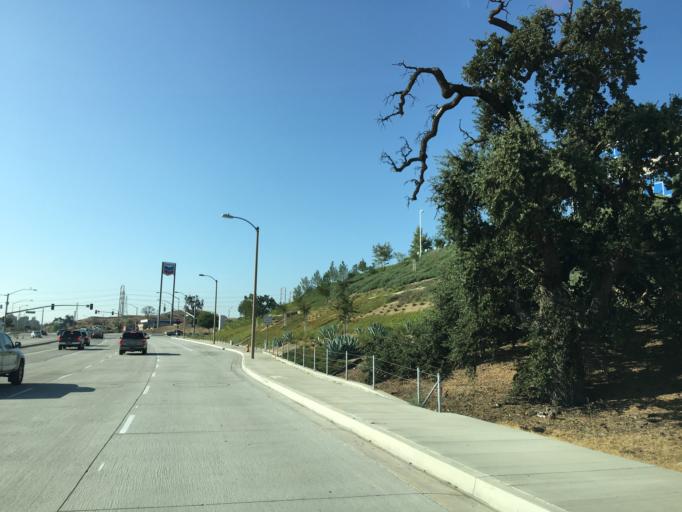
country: US
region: California
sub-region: Los Angeles County
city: Valencia
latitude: 34.4234
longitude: -118.5859
